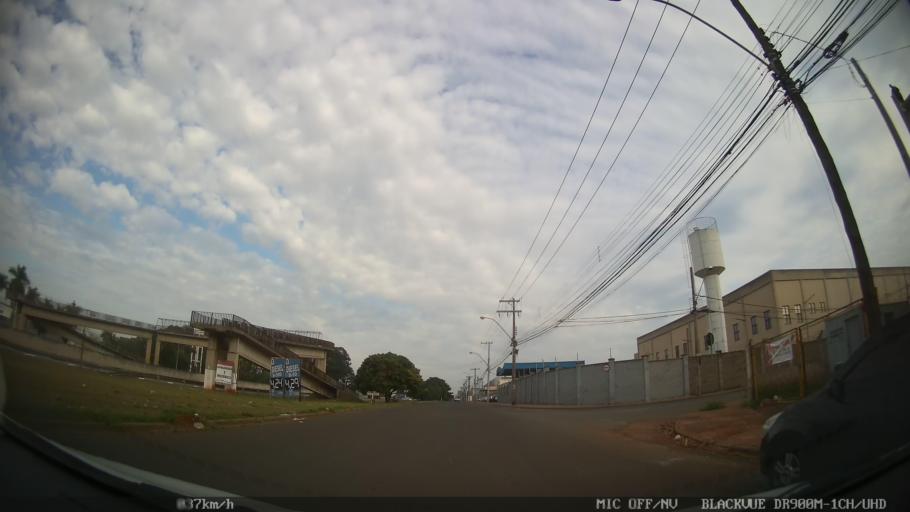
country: BR
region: Sao Paulo
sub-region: Santa Barbara D'Oeste
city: Santa Barbara d'Oeste
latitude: -22.7634
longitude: -47.3808
